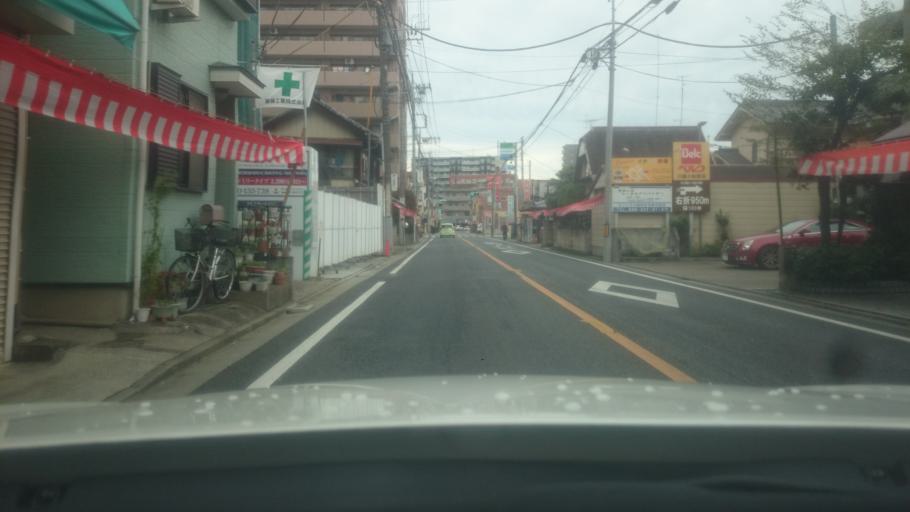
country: JP
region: Saitama
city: Kawagoe
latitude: 35.9147
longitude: 139.4854
